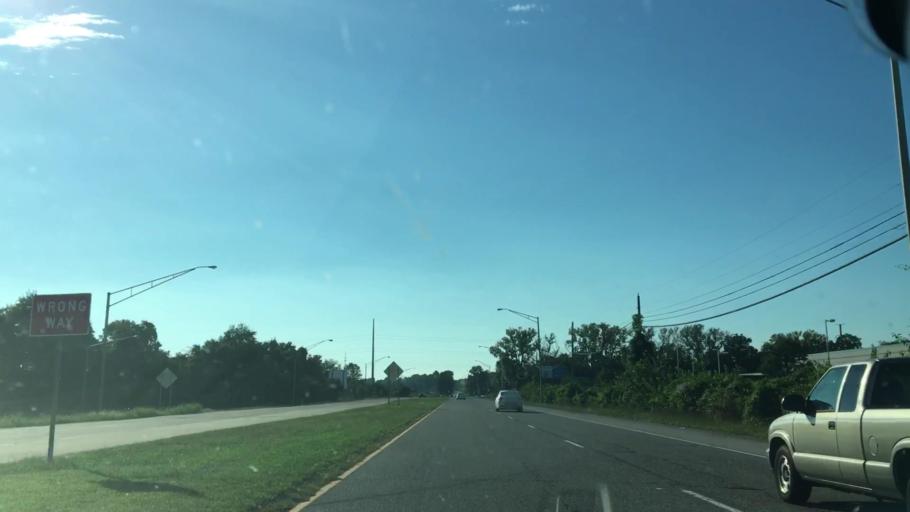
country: US
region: Kentucky
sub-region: Daviess County
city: Owensboro
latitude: 37.7754
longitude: -87.1664
